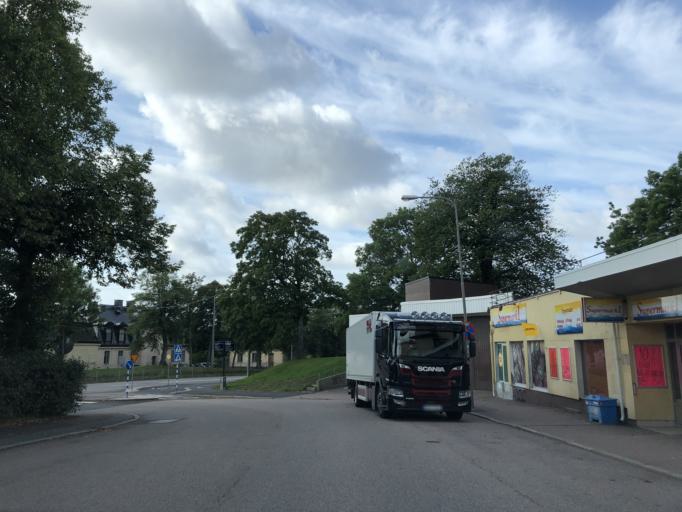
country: SE
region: Vaestra Goetaland
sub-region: Goteborg
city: Goeteborg
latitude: 57.7180
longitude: 12.0153
